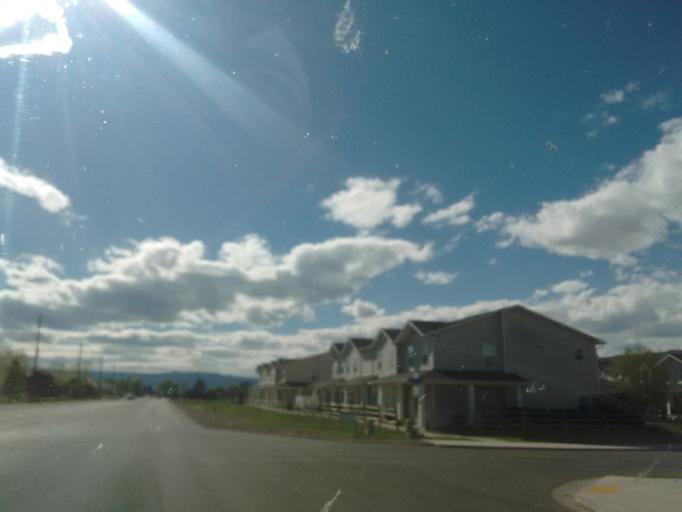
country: US
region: Colorado
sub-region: Mesa County
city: Fruitvale
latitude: 39.0629
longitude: -108.5057
